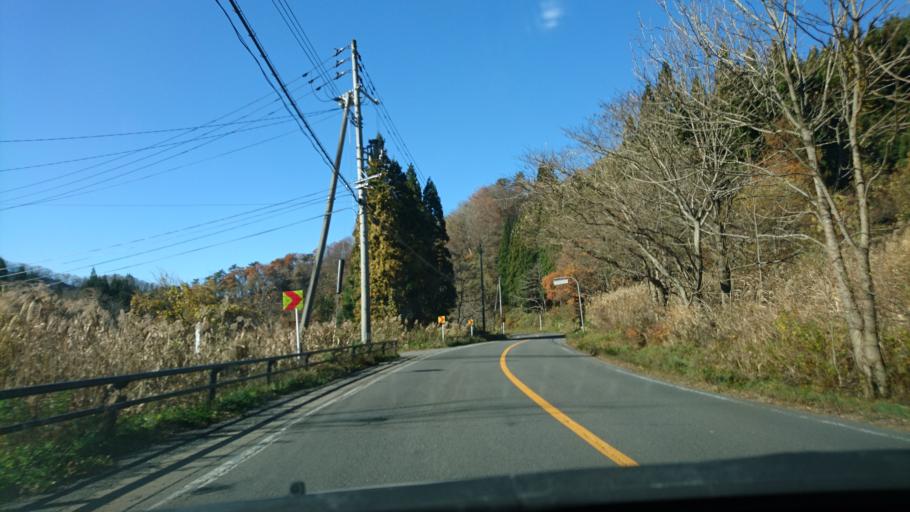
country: JP
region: Akita
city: Yokotemachi
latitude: 39.2819
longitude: 140.6736
